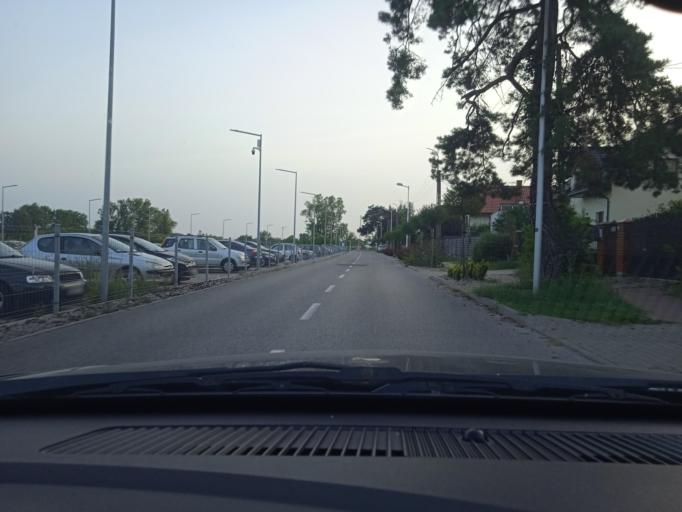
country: PL
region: Masovian Voivodeship
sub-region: Powiat nowodworski
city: Nowy Dwor Mazowiecki
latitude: 52.4436
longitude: 20.7022
